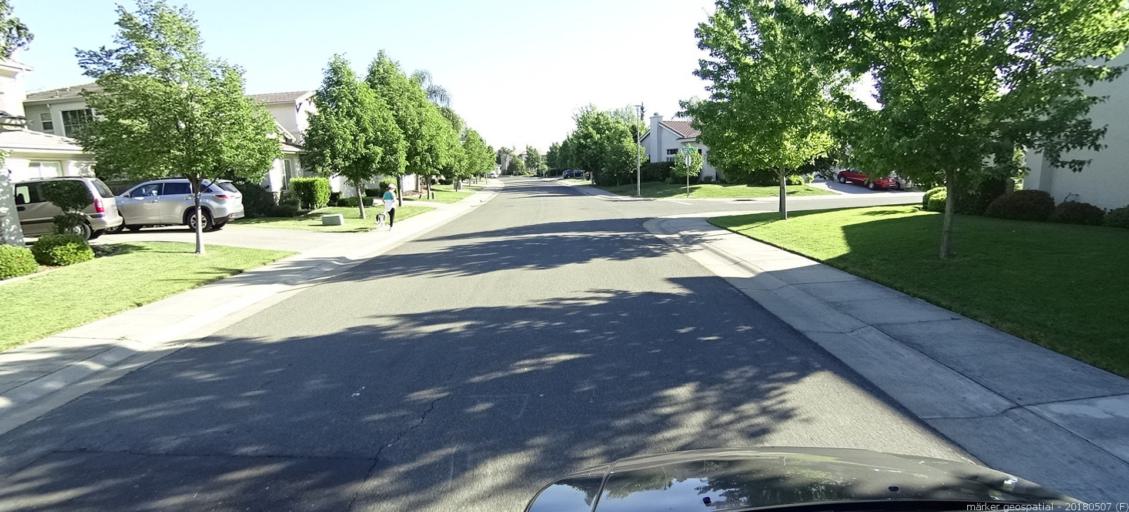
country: US
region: California
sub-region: Sacramento County
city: Rio Linda
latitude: 38.6682
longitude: -121.4971
